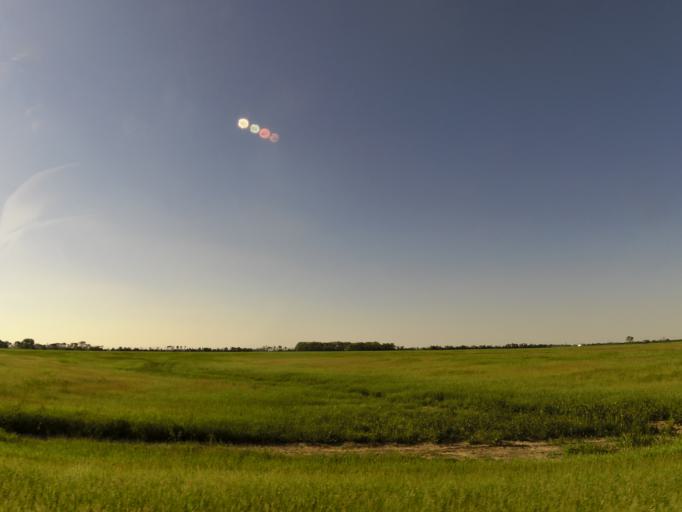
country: US
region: North Dakota
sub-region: Grand Forks County
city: Grand Forks Air Force Base
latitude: 48.1356
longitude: -97.1980
